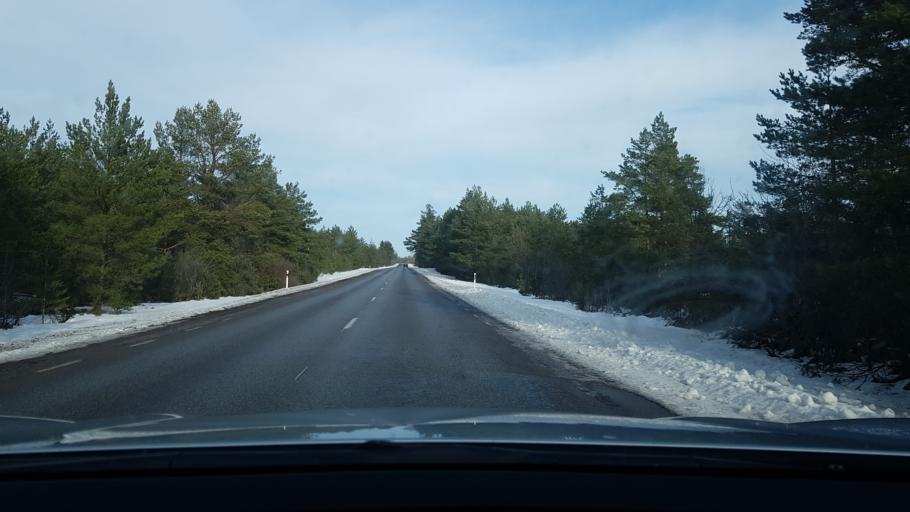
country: EE
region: Saare
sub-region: Kuressaare linn
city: Kuressaare
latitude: 58.3201
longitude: 22.5482
